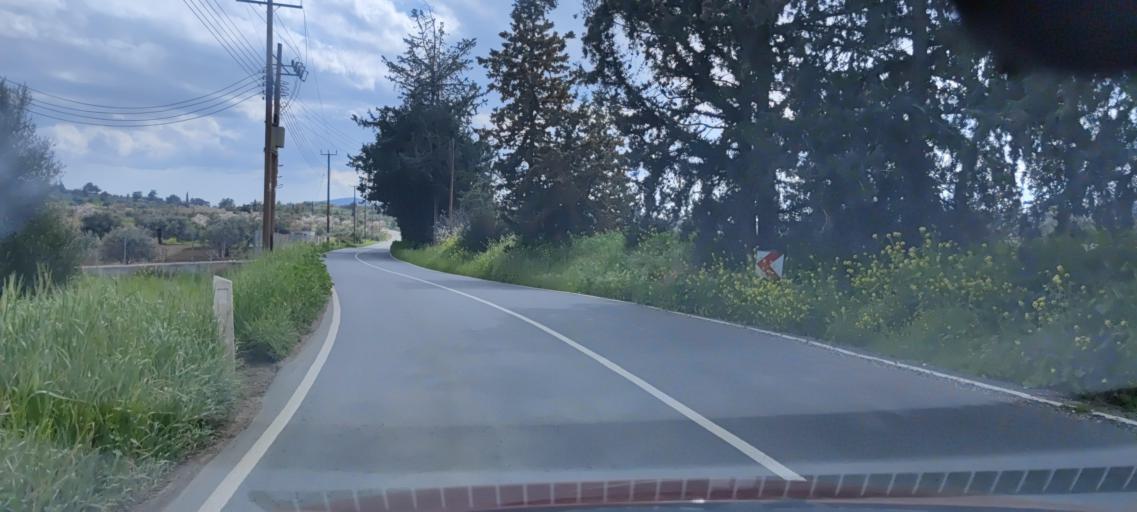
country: CY
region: Lefkosia
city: Lythrodontas
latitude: 34.9925
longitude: 33.2959
